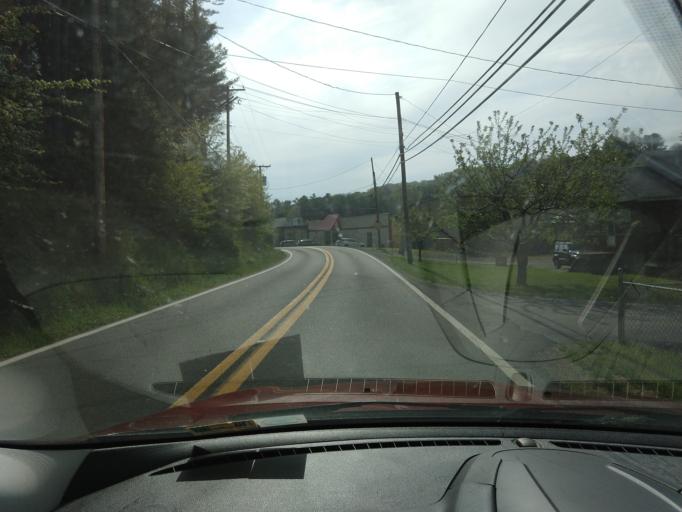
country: US
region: West Virginia
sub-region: Raleigh County
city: Crab Orchard
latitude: 37.7399
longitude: -81.2363
